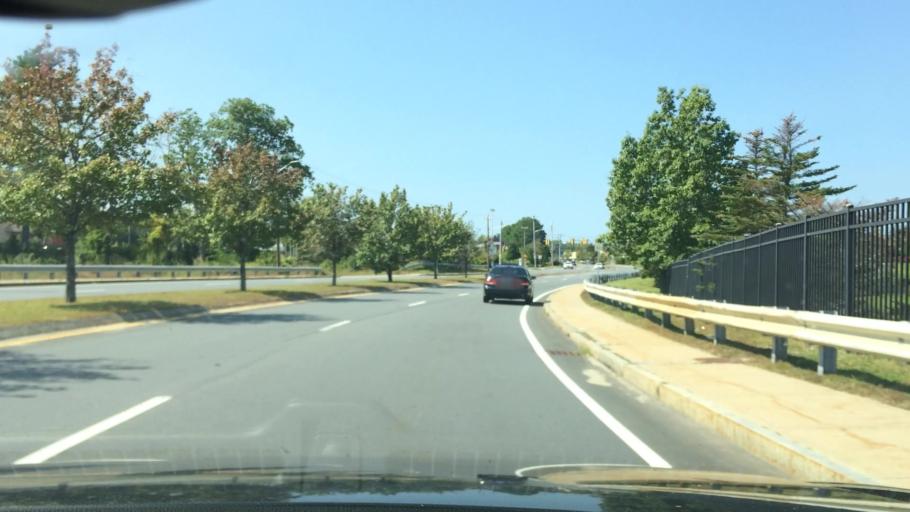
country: US
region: Massachusetts
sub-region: Essex County
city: Lawrence
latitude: 42.7419
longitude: -71.1586
